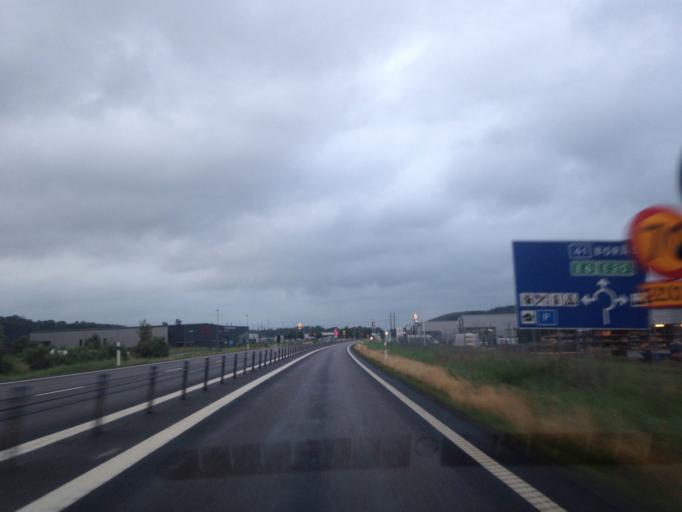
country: SE
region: Halland
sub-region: Varbergs Kommun
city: Varberg
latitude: 57.1633
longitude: 12.2739
